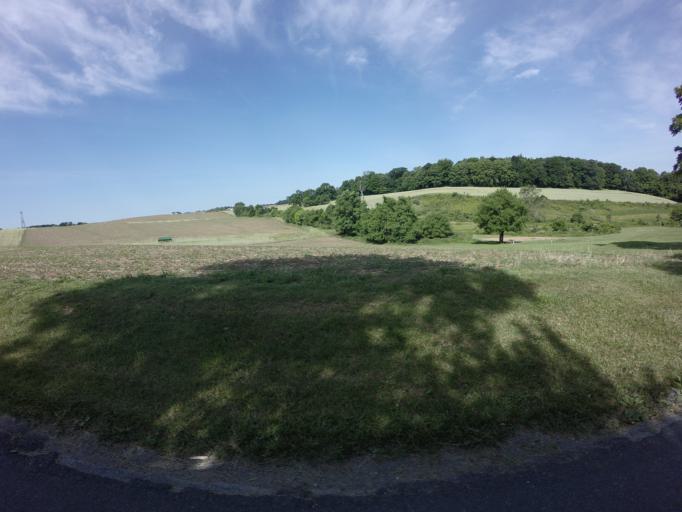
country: US
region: Maryland
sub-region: Frederick County
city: Green Valley
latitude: 39.3640
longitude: -77.2755
